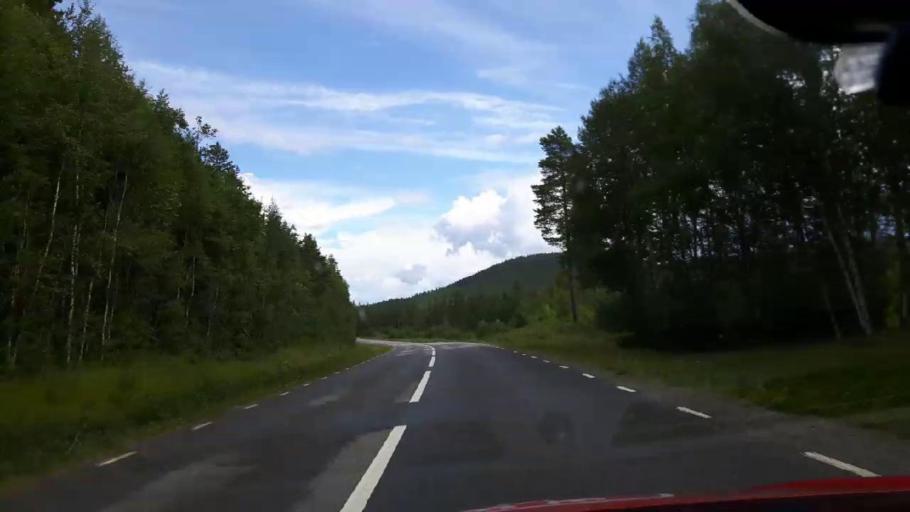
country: SE
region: Jaemtland
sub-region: Stroemsunds Kommun
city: Stroemsund
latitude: 64.3346
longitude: 14.9756
